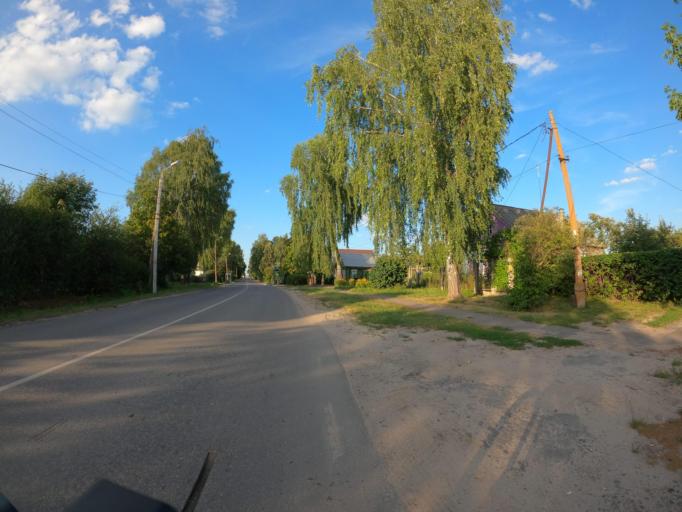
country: RU
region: Moskovskaya
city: Raduzhnyy
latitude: 55.1021
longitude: 38.7325
